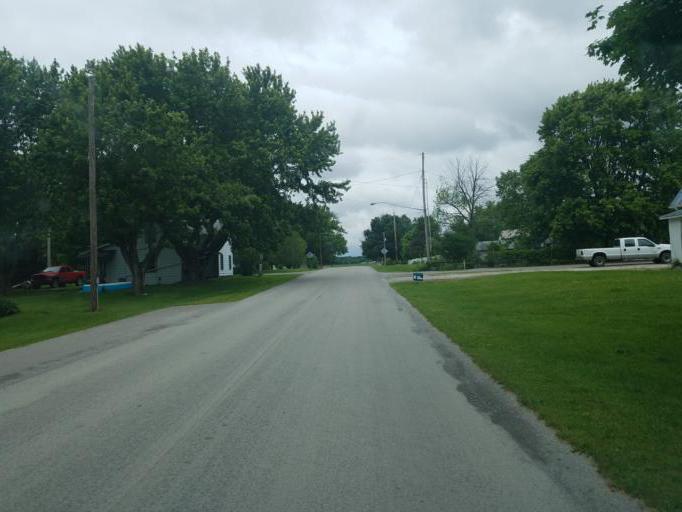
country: US
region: Ohio
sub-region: Wyandot County
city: Upper Sandusky
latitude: 40.7401
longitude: -83.2163
